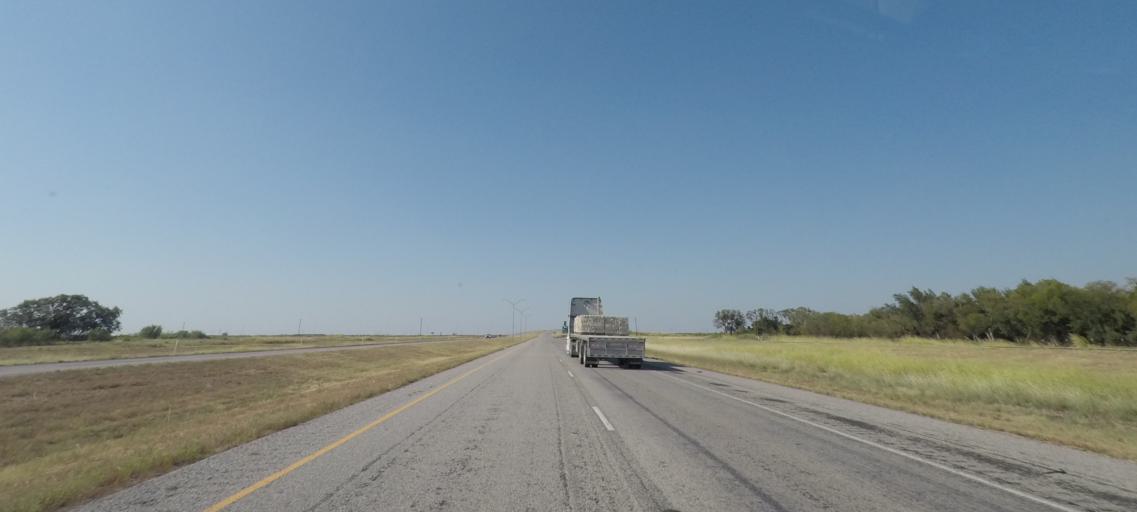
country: US
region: Texas
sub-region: Baylor County
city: Seymour
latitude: 33.6068
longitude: -99.2425
